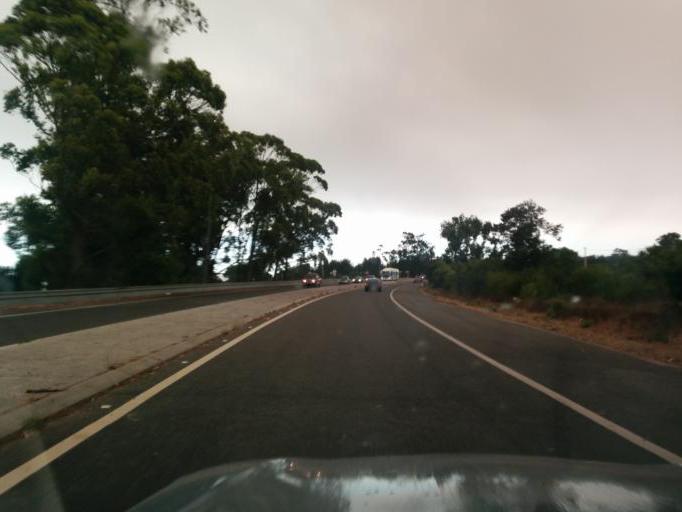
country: PT
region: Beja
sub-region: Odemira
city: Vila Nova de Milfontes
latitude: 37.7014
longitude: -8.7710
